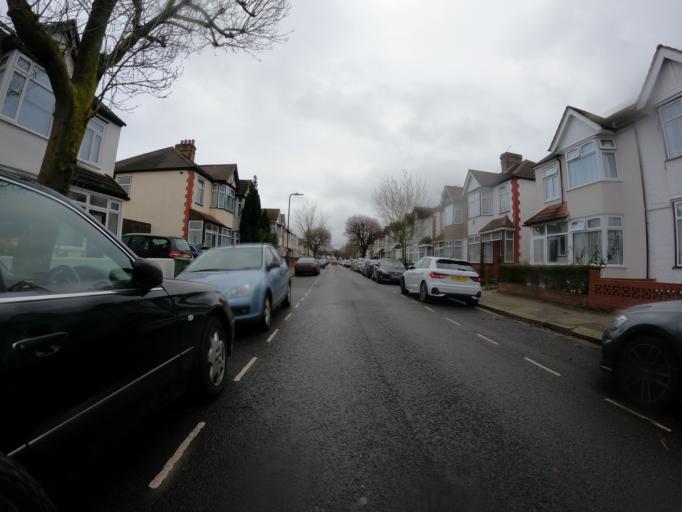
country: GB
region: England
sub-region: Greater London
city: Brentford
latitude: 51.5018
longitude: -0.3277
